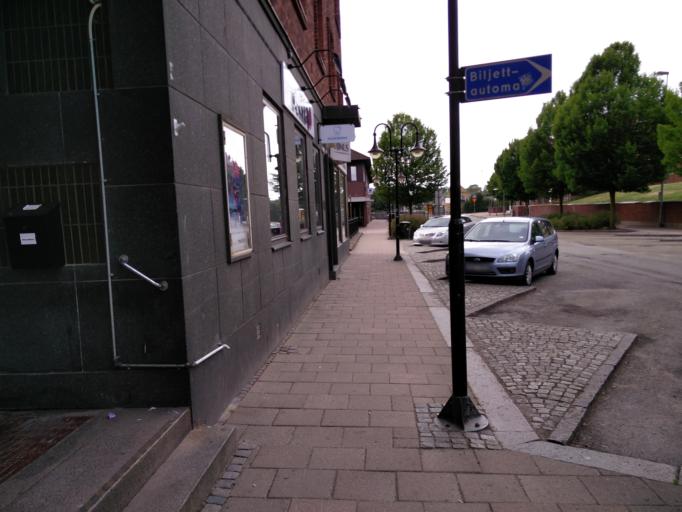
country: SE
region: Skane
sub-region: Hassleholms Kommun
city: Hassleholm
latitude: 56.1590
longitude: 13.7662
